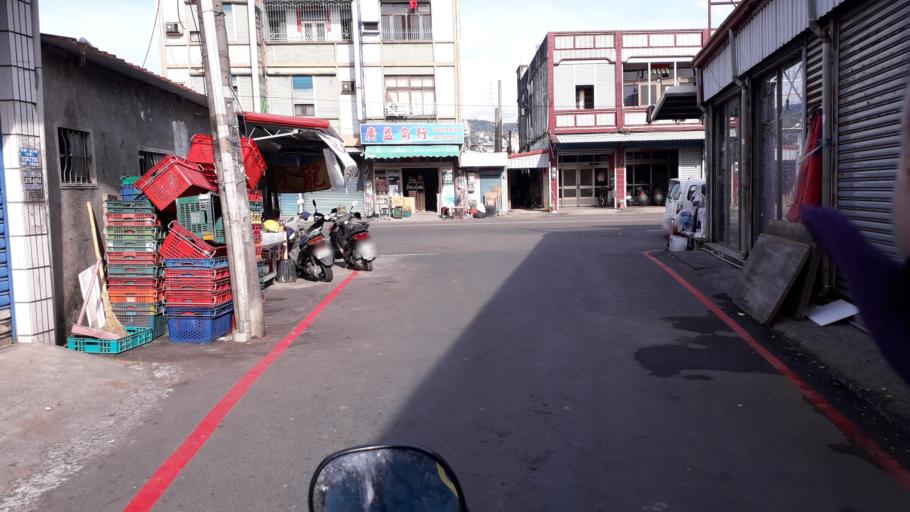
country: TW
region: Taiwan
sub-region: Pingtung
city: Pingtung
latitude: 22.3607
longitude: 120.5999
